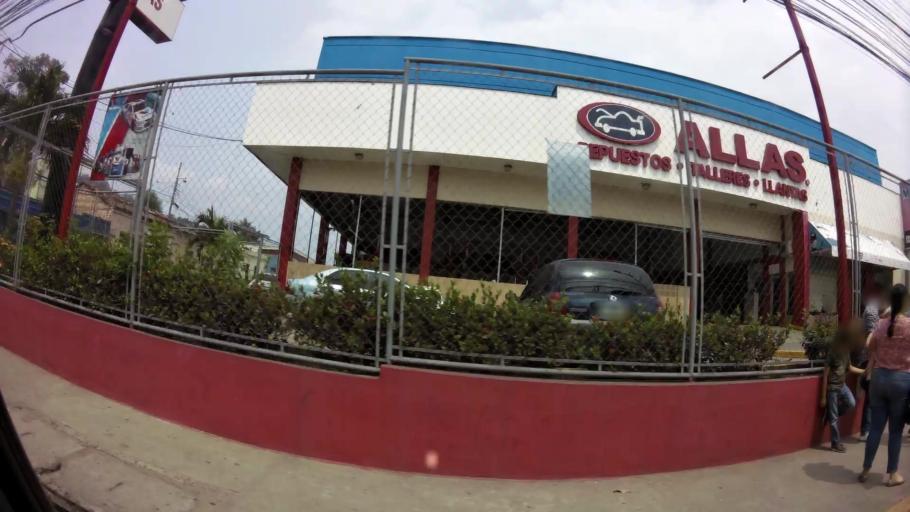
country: HN
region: Francisco Morazan
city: Tegucigalpa
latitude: 14.0894
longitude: -87.2076
